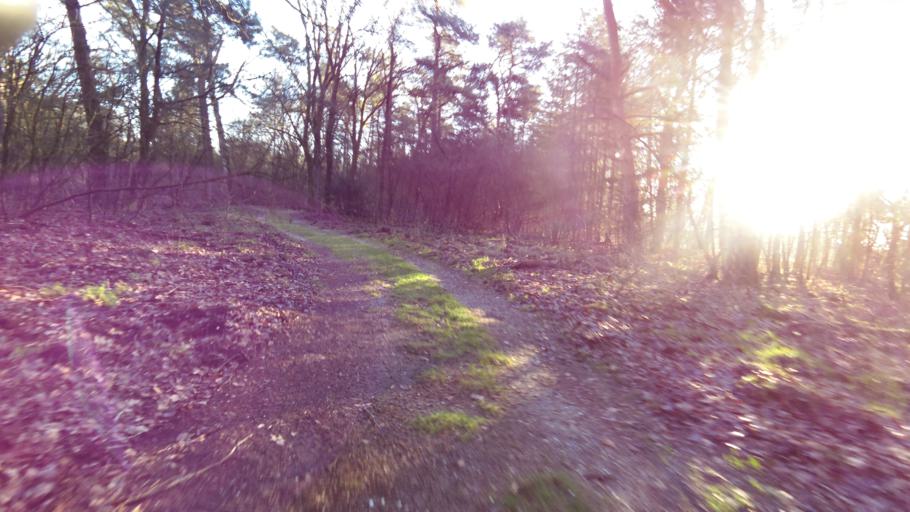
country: NL
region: Gelderland
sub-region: Gemeente Barneveld
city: Garderen
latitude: 52.2145
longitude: 5.7176
